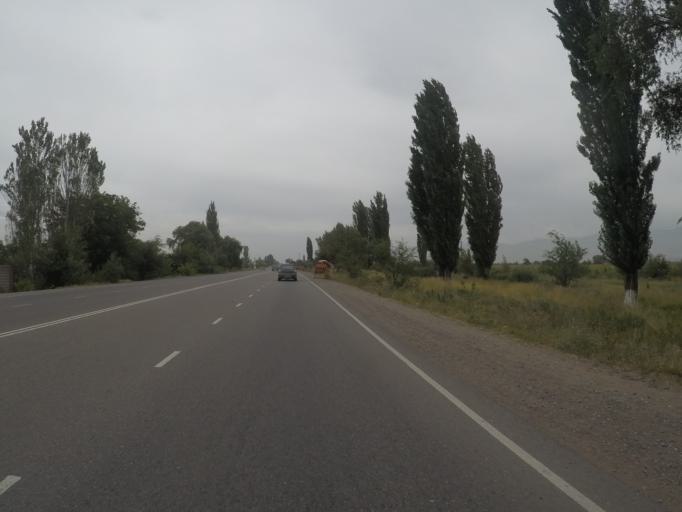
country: KG
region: Chuy
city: Bystrovka
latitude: 42.8206
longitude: 75.5685
